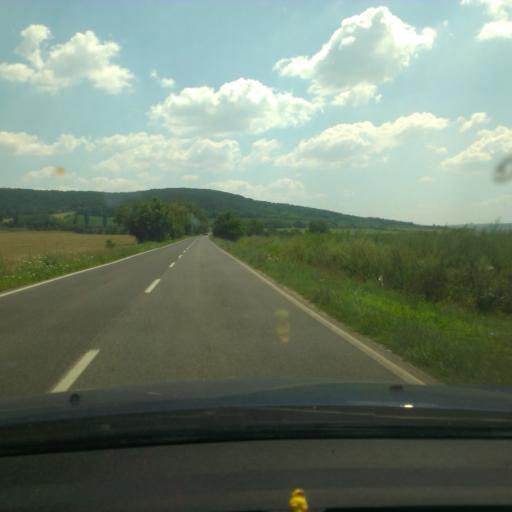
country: SK
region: Trnavsky
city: Hlohovec
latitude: 48.4684
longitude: 17.8118
